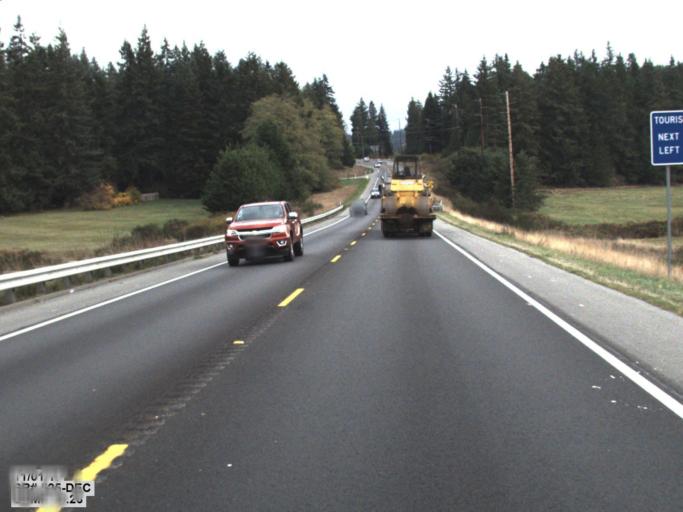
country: US
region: Washington
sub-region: Island County
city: Freeland
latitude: 48.0069
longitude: -122.4923
